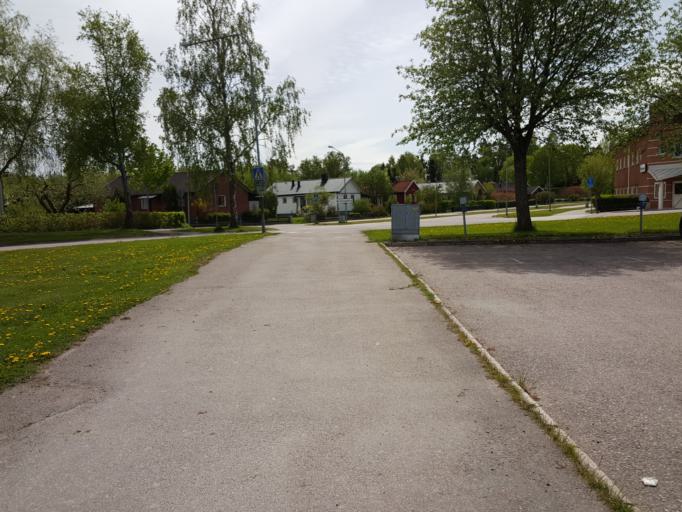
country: SE
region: Uppsala
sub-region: Osthammars Kommun
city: Gimo
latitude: 60.1721
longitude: 18.1856
